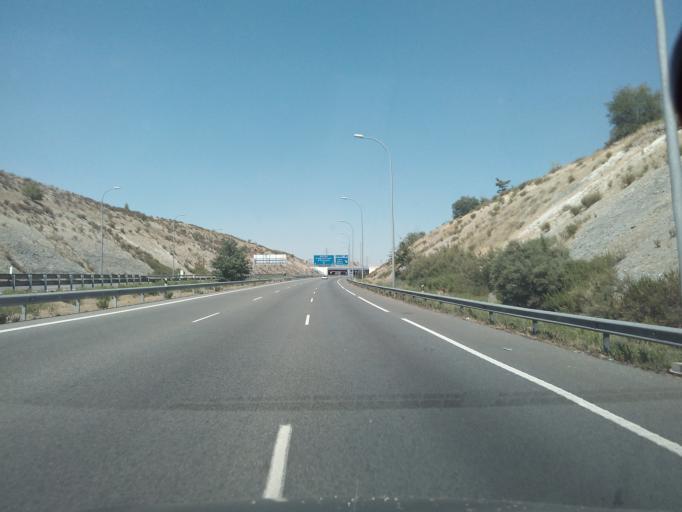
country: ES
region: Madrid
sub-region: Provincia de Madrid
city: Villa de Vallecas
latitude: 40.3740
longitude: -3.5530
